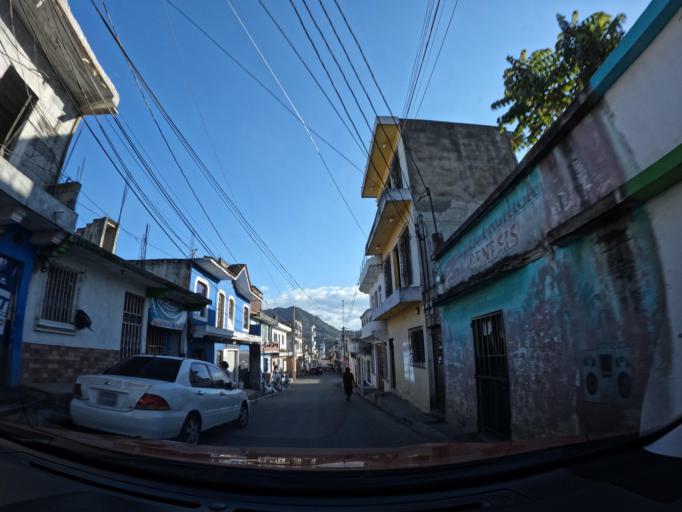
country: GT
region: Escuintla
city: Palin
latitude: 14.4060
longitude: -90.6985
